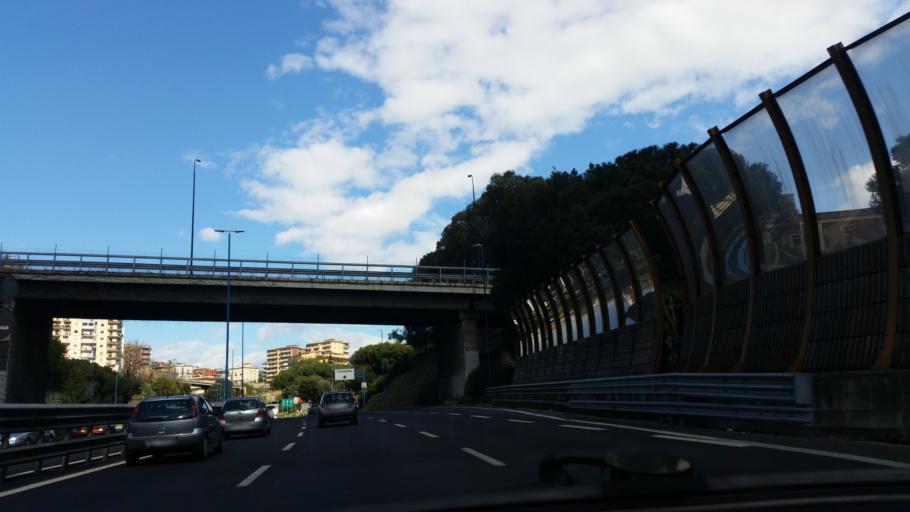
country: IT
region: Campania
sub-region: Provincia di Napoli
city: Napoli
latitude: 40.8537
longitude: 14.2184
